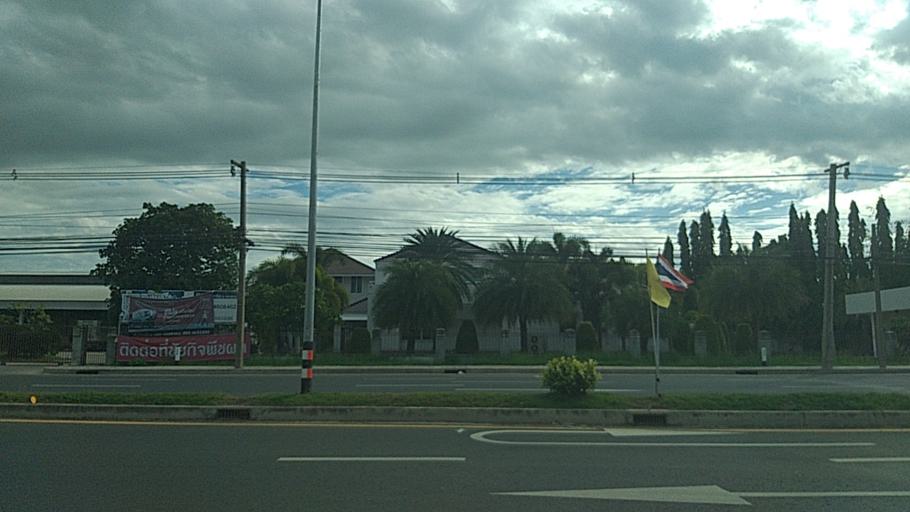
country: TH
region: Surin
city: Prasat
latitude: 14.6222
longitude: 103.4120
